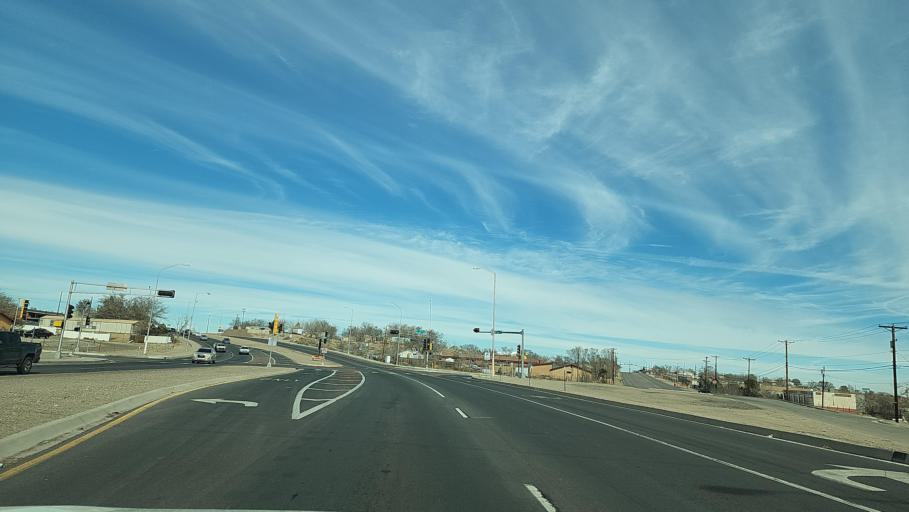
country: US
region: New Mexico
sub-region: Bernalillo County
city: South Valley
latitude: 35.0560
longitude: -106.7056
